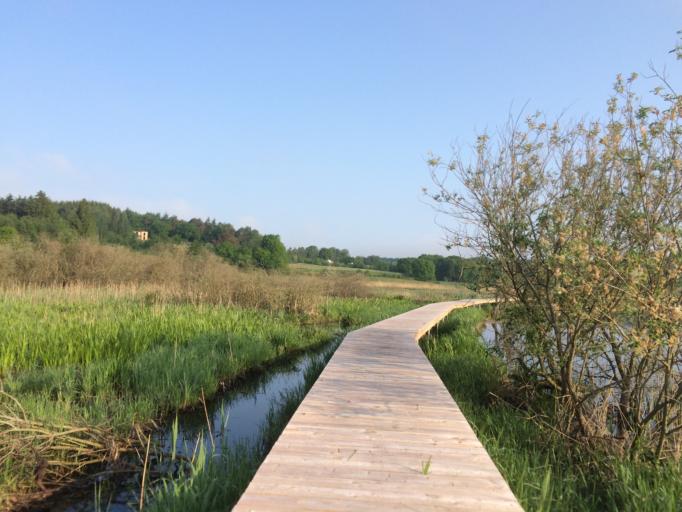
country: DK
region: Central Jutland
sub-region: Silkeborg Kommune
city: Svejbaek
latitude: 56.1969
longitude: 9.6499
